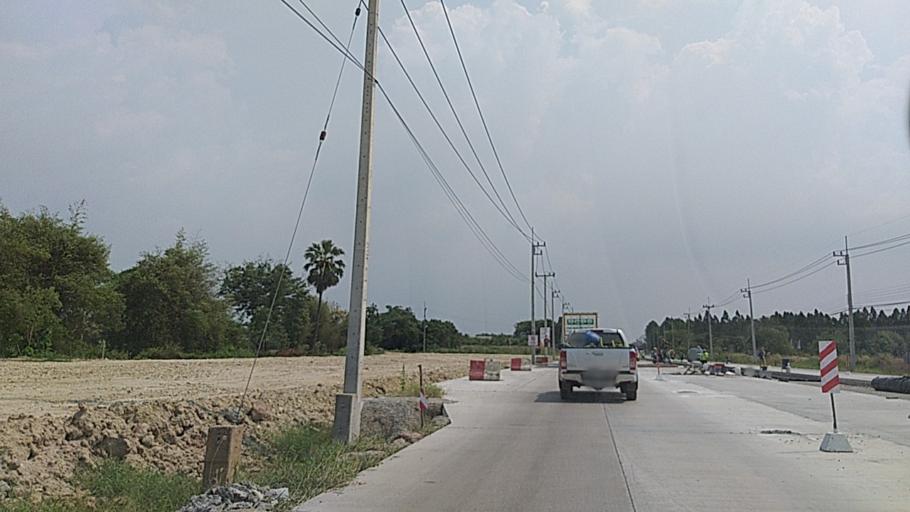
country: TH
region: Chon Buri
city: Phanat Nikhom
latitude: 13.3788
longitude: 101.1943
